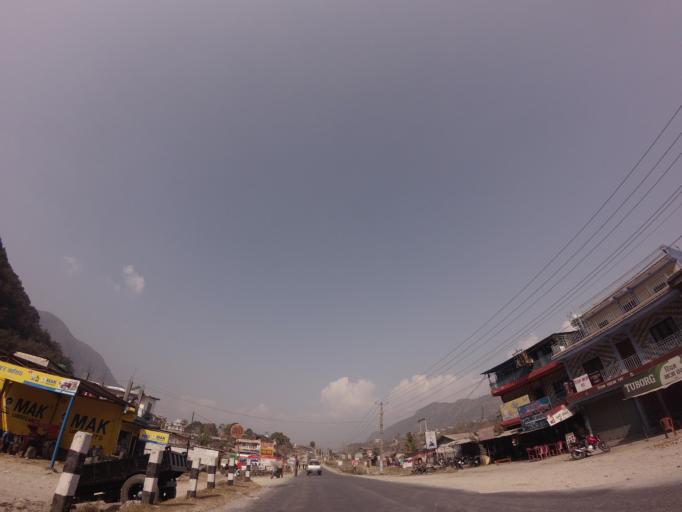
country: NP
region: Western Region
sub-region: Gandaki Zone
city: Pokhara
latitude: 28.2542
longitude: 83.9665
